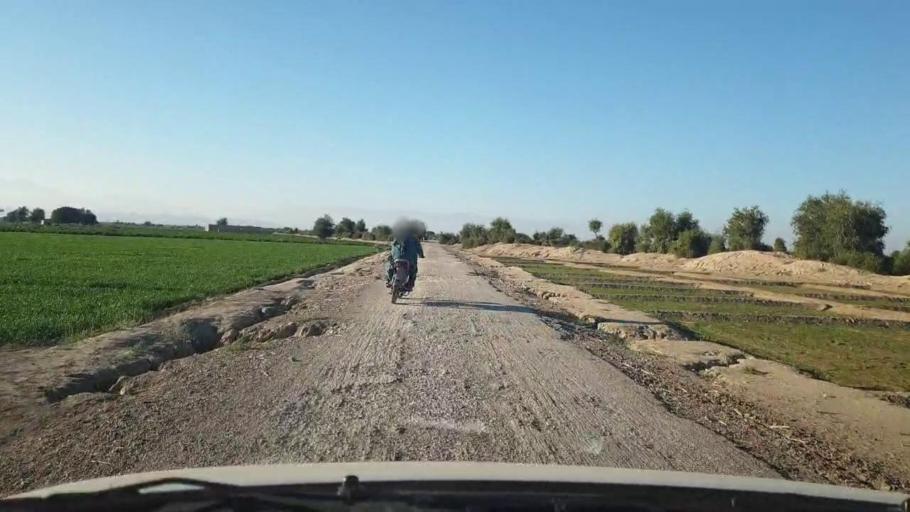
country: PK
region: Sindh
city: Johi
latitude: 26.7647
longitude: 67.4645
